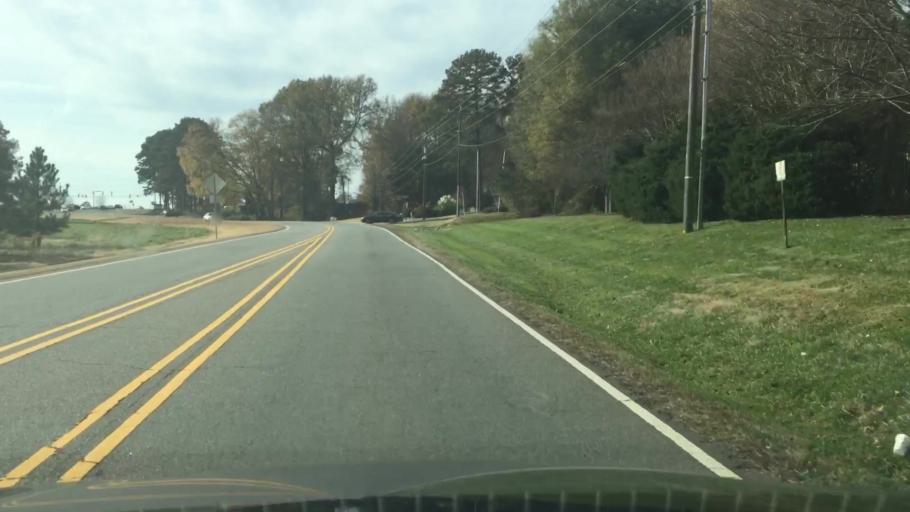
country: US
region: North Carolina
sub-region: Iredell County
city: Mooresville
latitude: 35.5798
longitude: -80.8364
